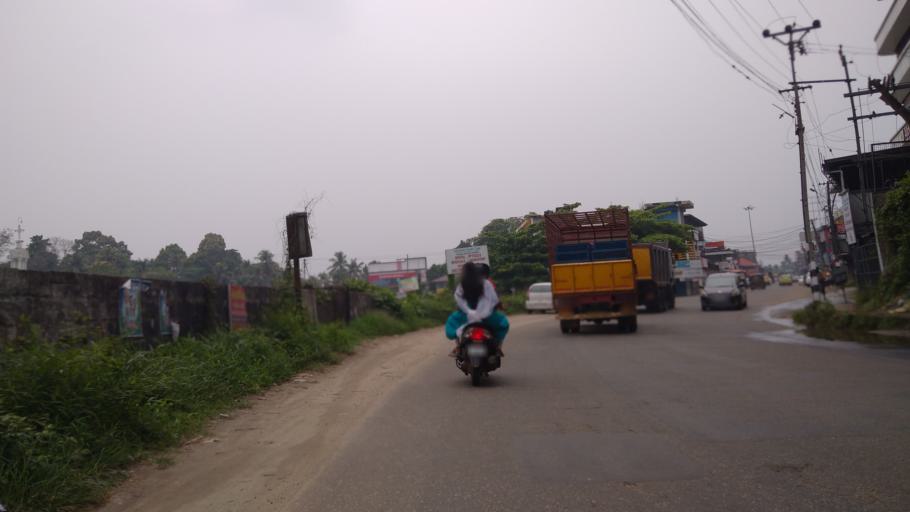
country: IN
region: Kerala
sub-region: Ernakulam
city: Perumpavur
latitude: 10.1115
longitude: 76.5202
